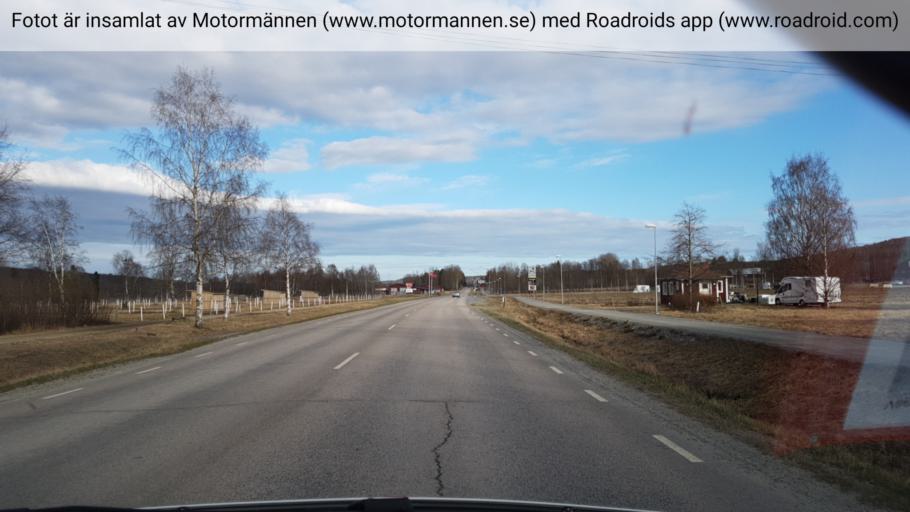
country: SE
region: Vaesternorrland
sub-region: OErnskoeldsviks Kommun
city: Ornskoldsvik
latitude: 63.2858
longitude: 18.6289
